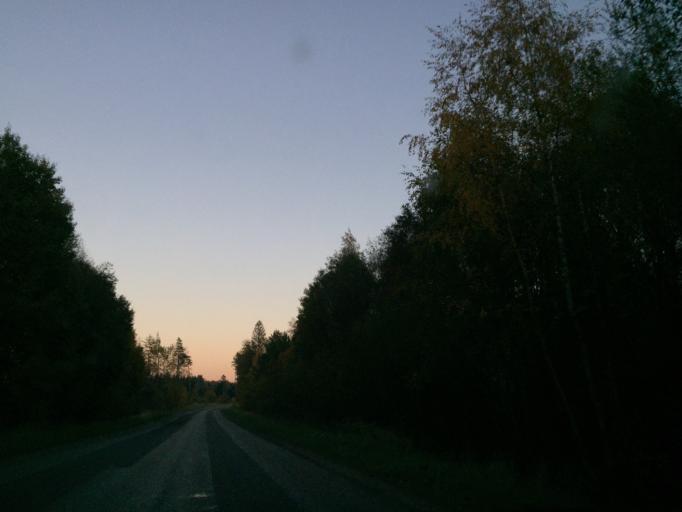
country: LT
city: Vieksniai
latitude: 56.3946
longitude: 22.5657
